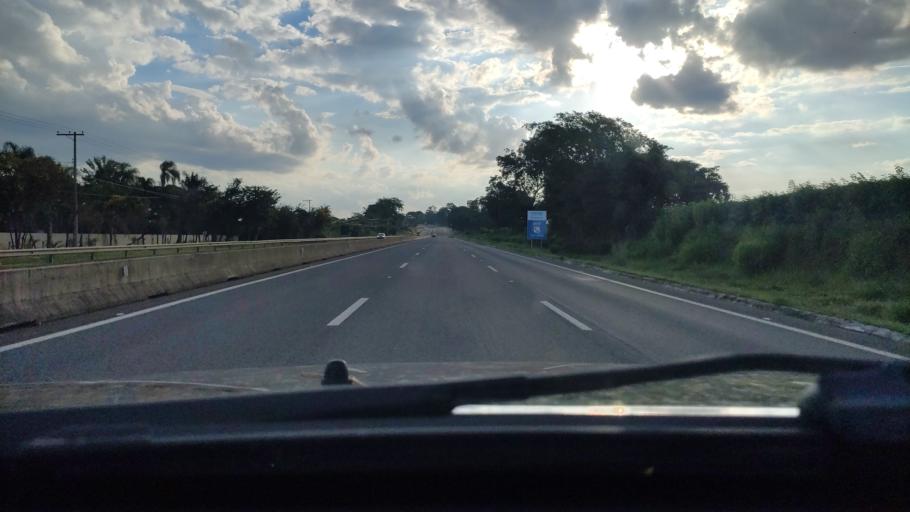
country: BR
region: Sao Paulo
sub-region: Mogi-Mirim
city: Mogi Mirim
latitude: -22.4505
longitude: -47.0749
